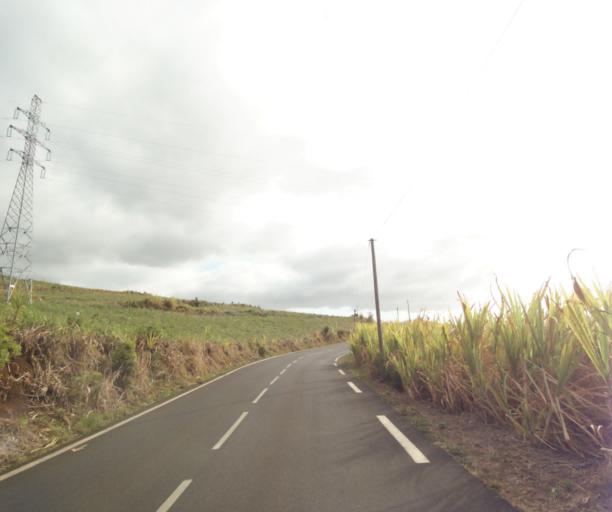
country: RE
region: Reunion
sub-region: Reunion
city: Saint-Paul
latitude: -21.0261
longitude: 55.3131
